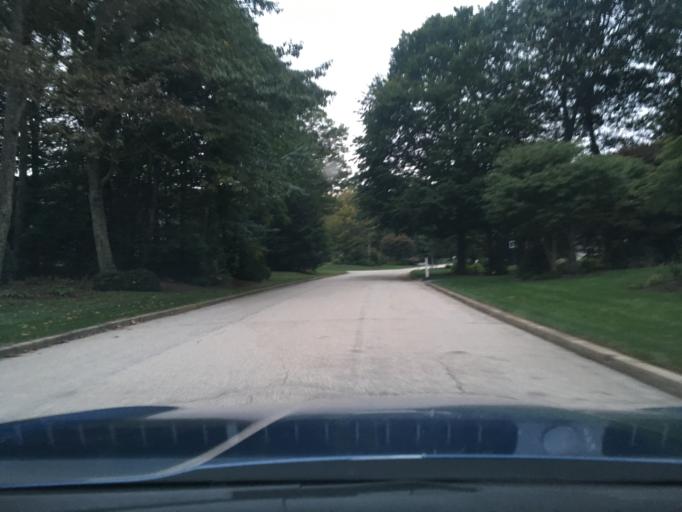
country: US
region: Rhode Island
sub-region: Kent County
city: West Warwick
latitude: 41.6529
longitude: -71.5127
